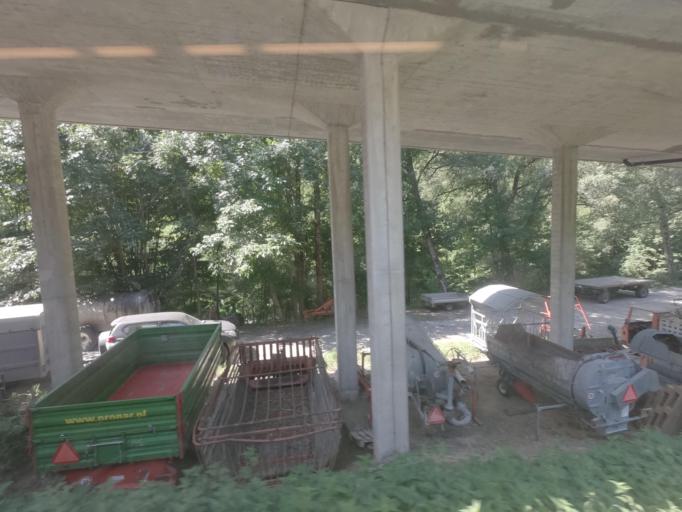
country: CH
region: Valais
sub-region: Entremont District
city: Bagnes
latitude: 46.0817
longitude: 7.2117
